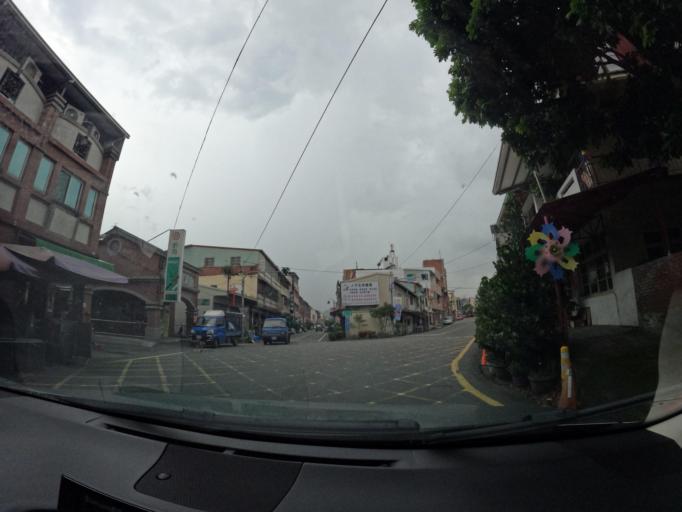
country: TW
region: Taiwan
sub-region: Nantou
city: Nantou
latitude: 23.8786
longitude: 120.7688
